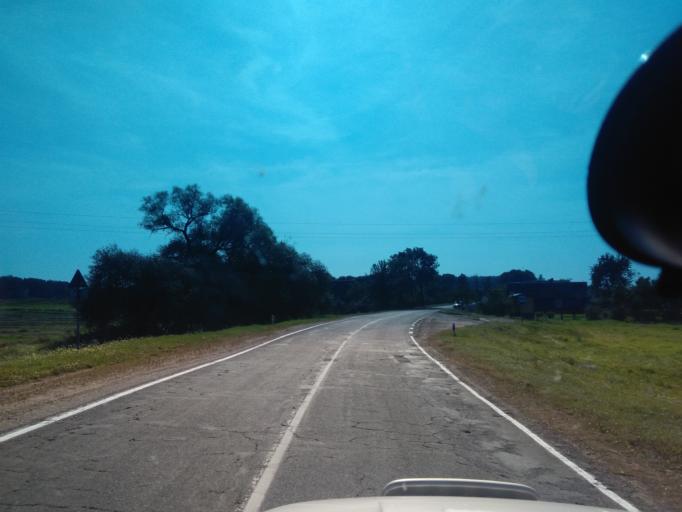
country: BY
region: Minsk
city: Uzda
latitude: 53.3900
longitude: 27.2423
